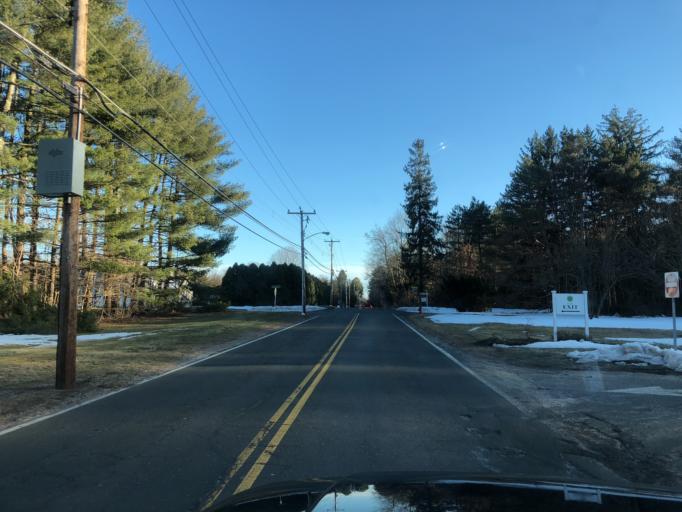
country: US
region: Connecticut
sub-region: Hartford County
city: Farmington
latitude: 41.7666
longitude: -72.8589
